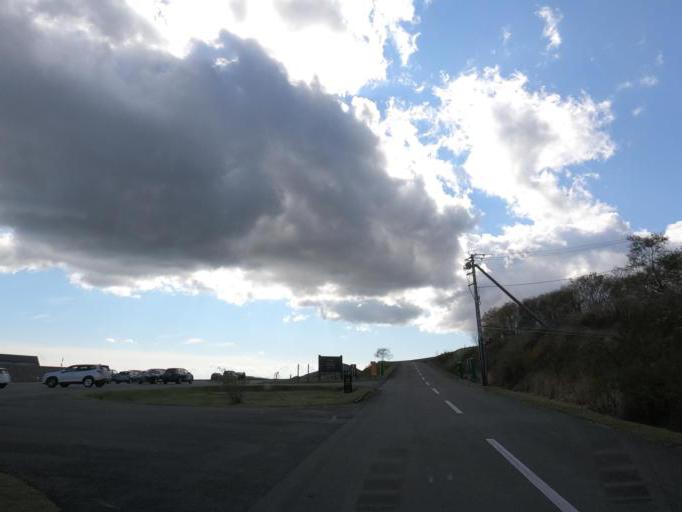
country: JP
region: Hokkaido
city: Otofuke
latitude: 43.2872
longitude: 143.1853
